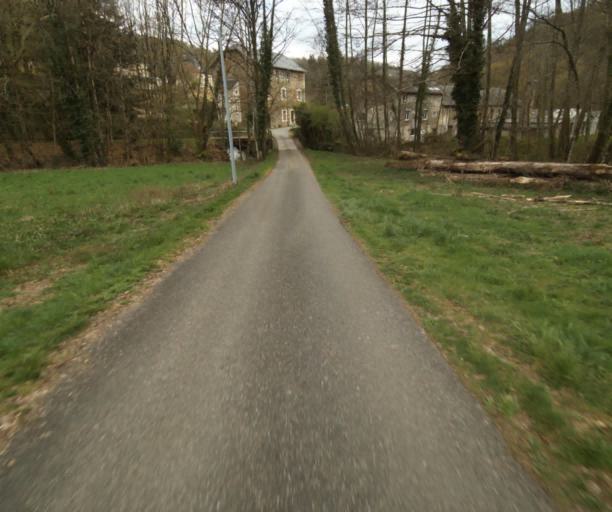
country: FR
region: Limousin
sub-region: Departement de la Correze
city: Tulle
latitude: 45.2565
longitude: 1.7752
